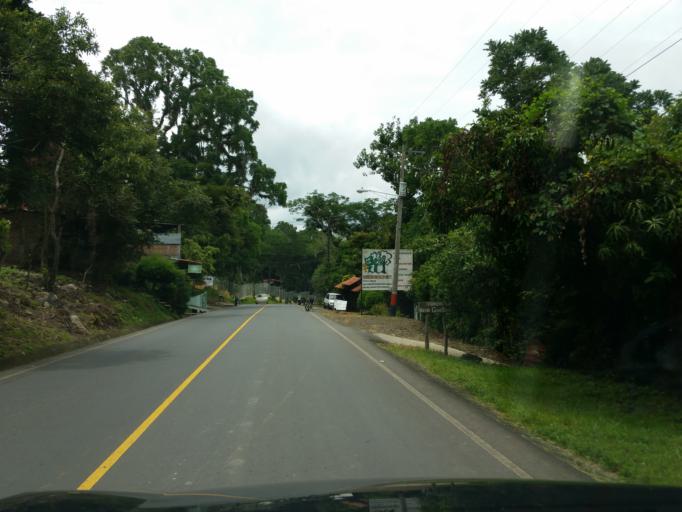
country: NI
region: Matagalpa
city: Matagalpa
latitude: 12.9633
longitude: -85.9195
